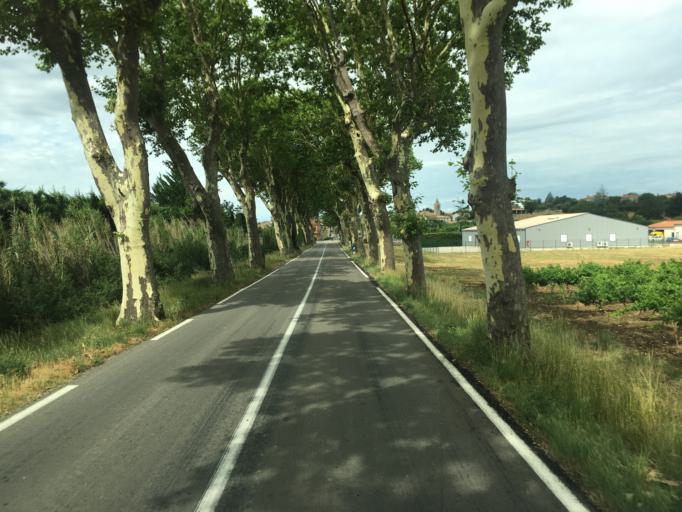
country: FR
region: Rhone-Alpes
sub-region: Departement de la Drome
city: Vinsobres
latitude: 44.2996
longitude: 5.0156
